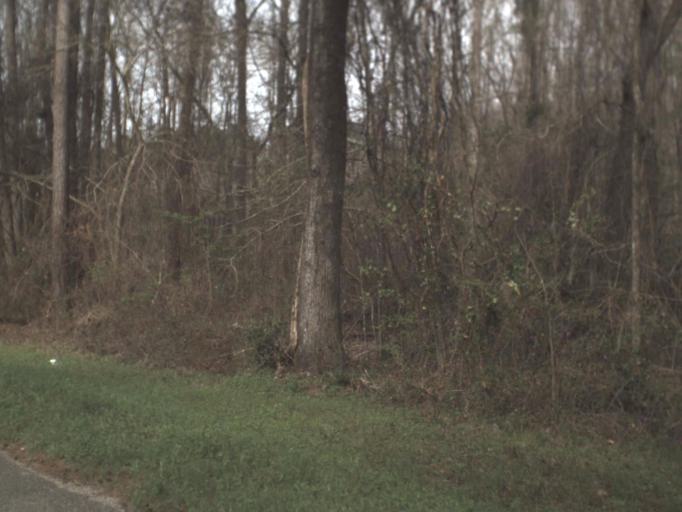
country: US
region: Florida
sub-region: Jefferson County
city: Monticello
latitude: 30.5217
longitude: -84.0687
